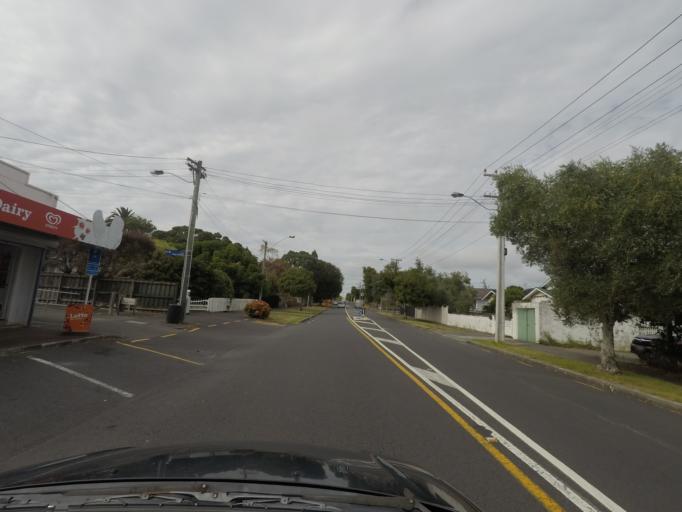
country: NZ
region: Auckland
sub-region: Auckland
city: Rosebank
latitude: -36.8839
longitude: 174.7104
